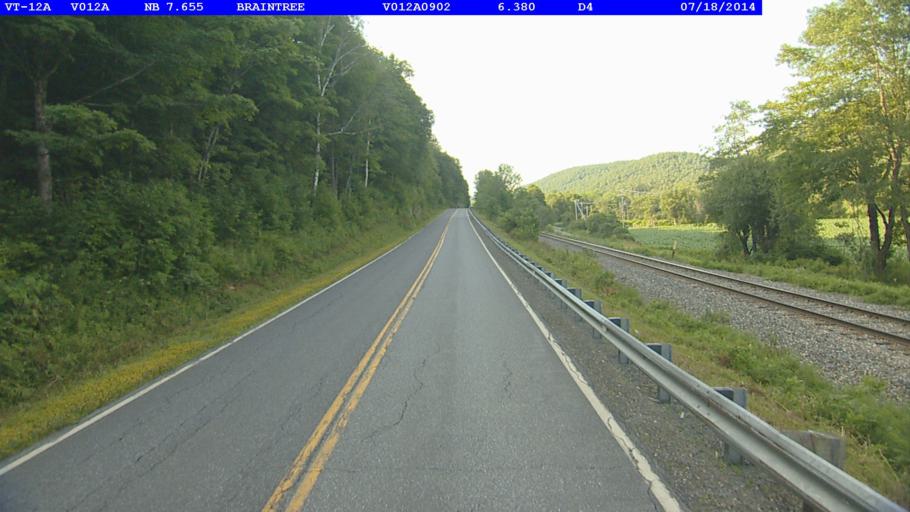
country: US
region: Vermont
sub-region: Orange County
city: Randolph
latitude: 43.9991
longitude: -72.7527
